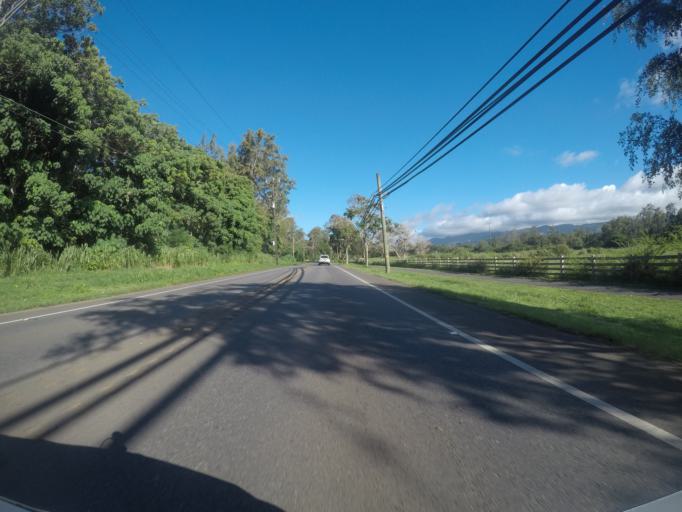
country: US
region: Hawaii
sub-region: Honolulu County
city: La'ie
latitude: 21.6582
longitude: -157.9319
